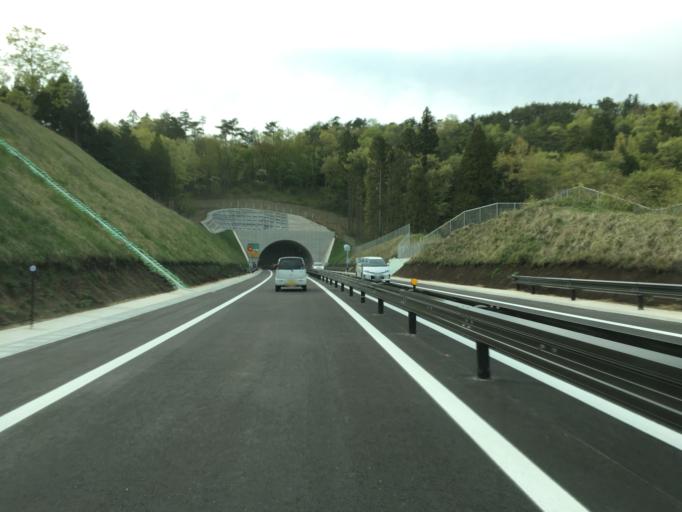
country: JP
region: Fukushima
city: Hobaramachi
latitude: 37.7770
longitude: 140.5810
